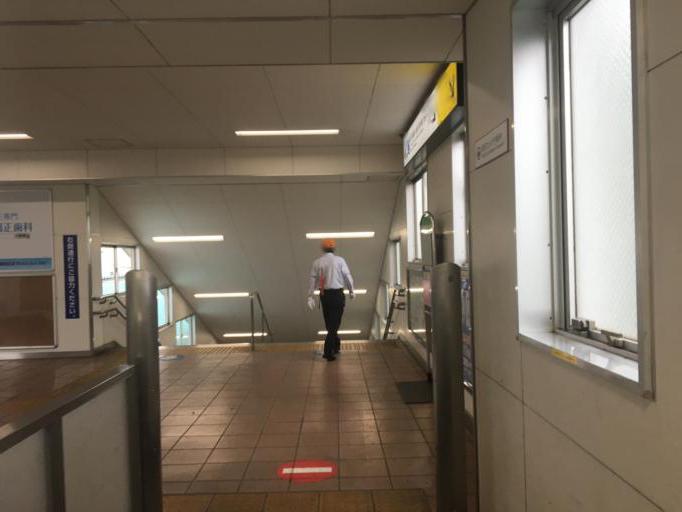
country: JP
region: Saitama
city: Tokorozawa
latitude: 35.7786
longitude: 139.4967
